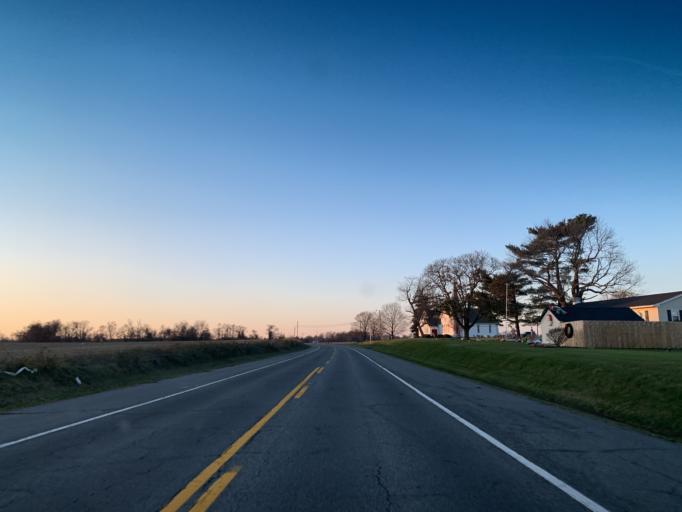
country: US
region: Maryland
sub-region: Cecil County
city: Charlestown
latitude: 39.4272
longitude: -75.9221
